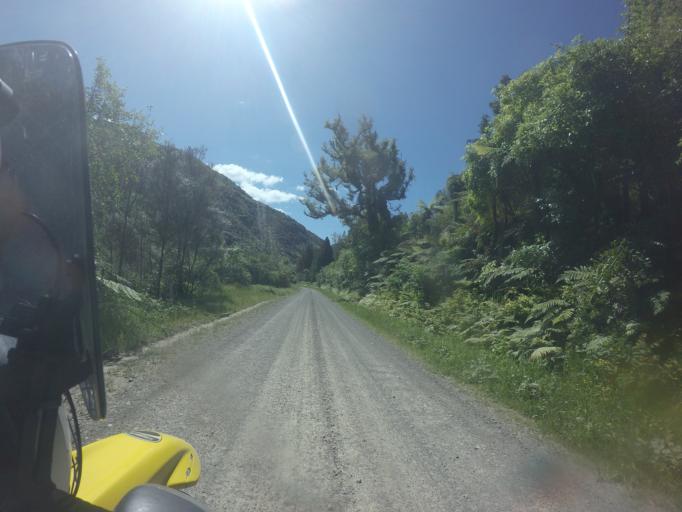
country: NZ
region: Bay of Plenty
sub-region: Opotiki District
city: Opotiki
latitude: -38.2829
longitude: 177.3416
